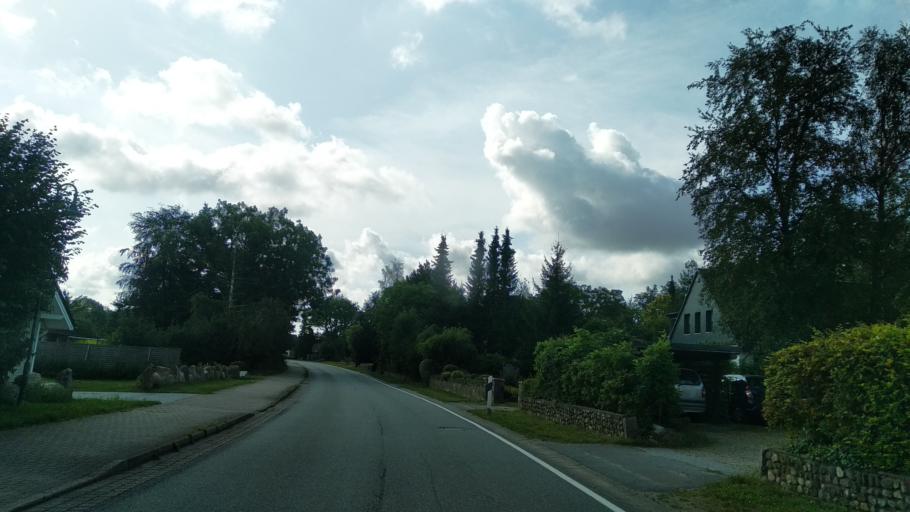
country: DE
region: Schleswig-Holstein
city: Selk
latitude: 54.4713
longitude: 9.5674
